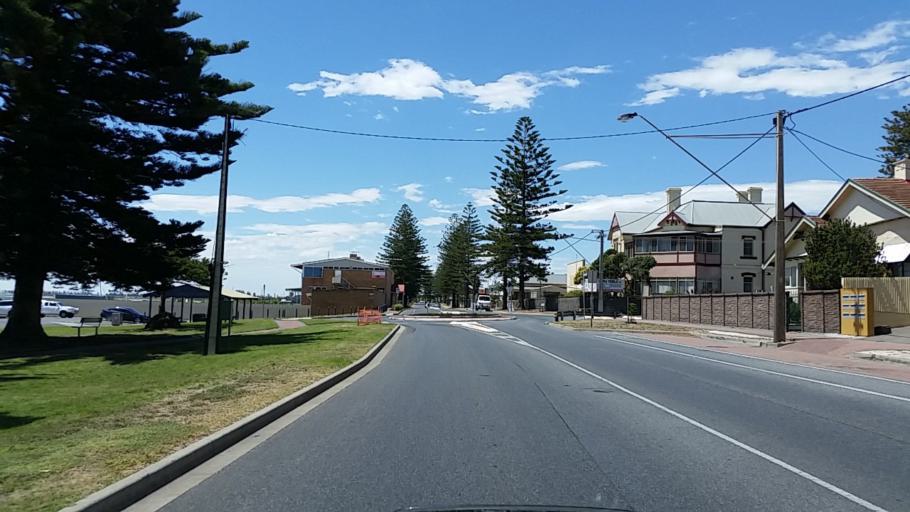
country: AU
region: South Australia
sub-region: Port Adelaide Enfield
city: Birkenhead
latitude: -34.8250
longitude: 138.4867
